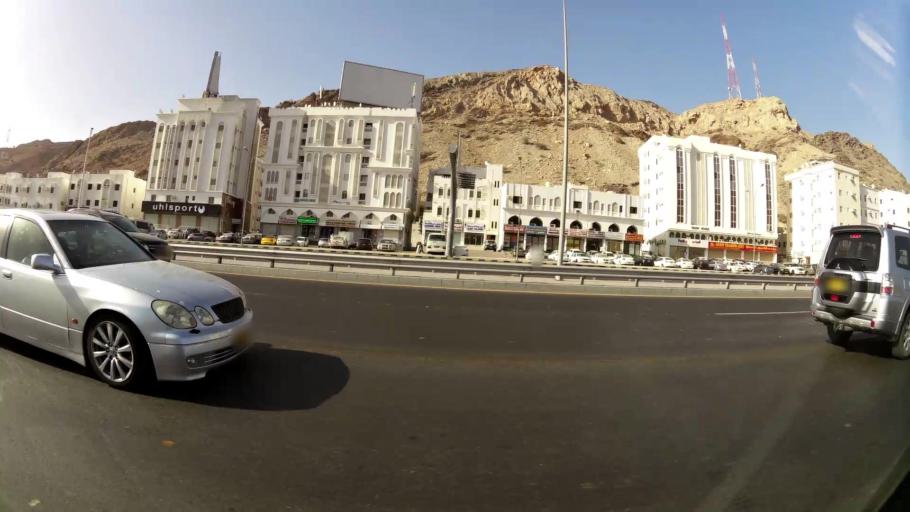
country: OM
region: Muhafazat Masqat
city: Muscat
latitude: 23.5904
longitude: 58.5309
